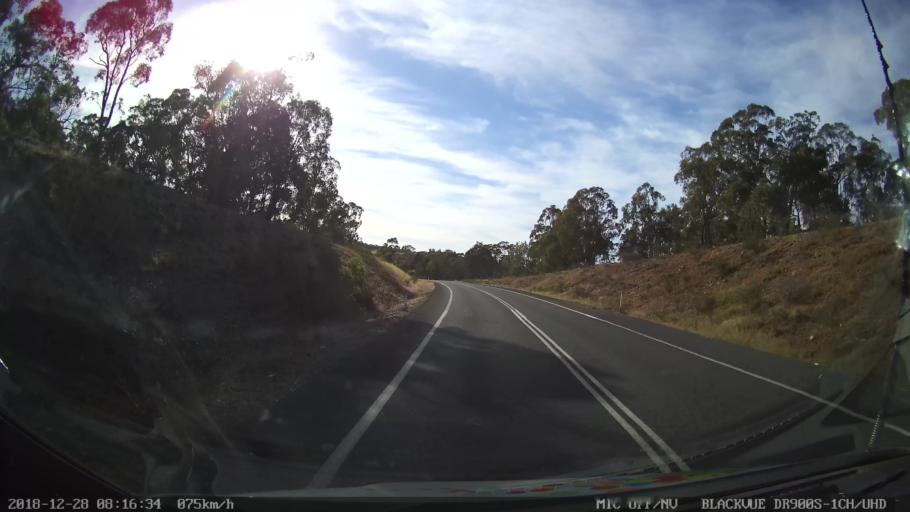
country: AU
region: New South Wales
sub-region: Blayney
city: Blayney
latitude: -33.8349
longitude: 149.3302
